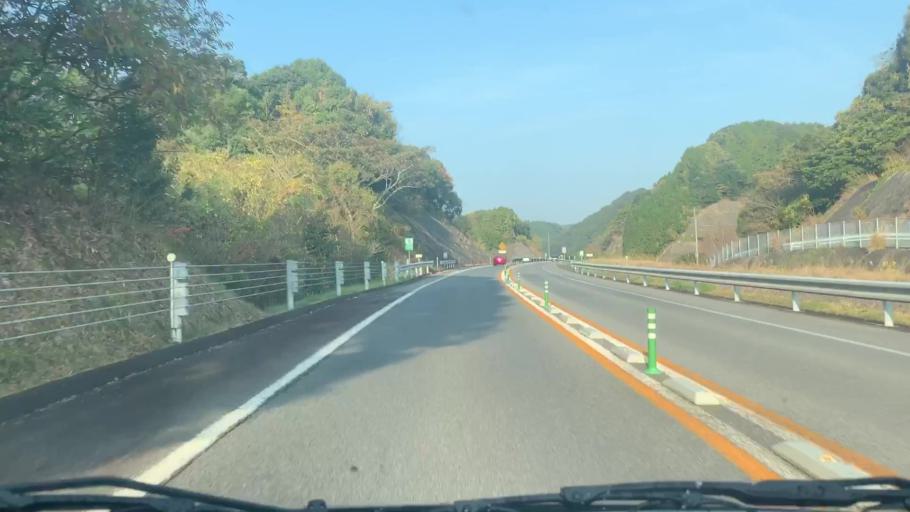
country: JP
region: Saga Prefecture
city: Ureshinomachi-shimojuku
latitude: 33.1443
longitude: 129.9531
